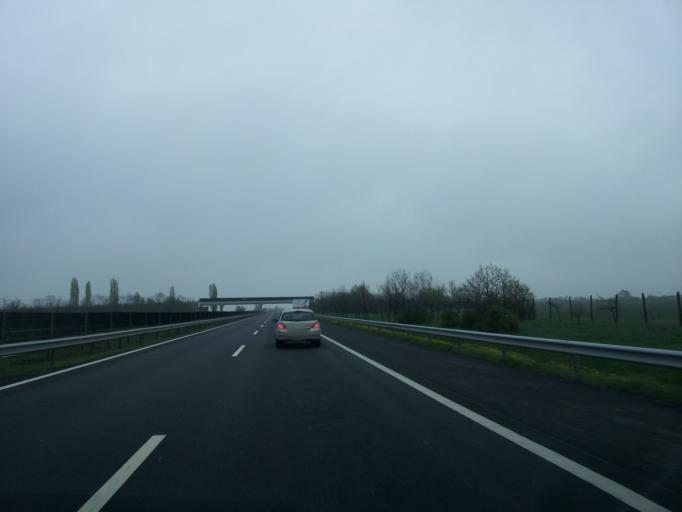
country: HU
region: Heves
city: Kompolt
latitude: 47.7088
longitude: 20.1845
